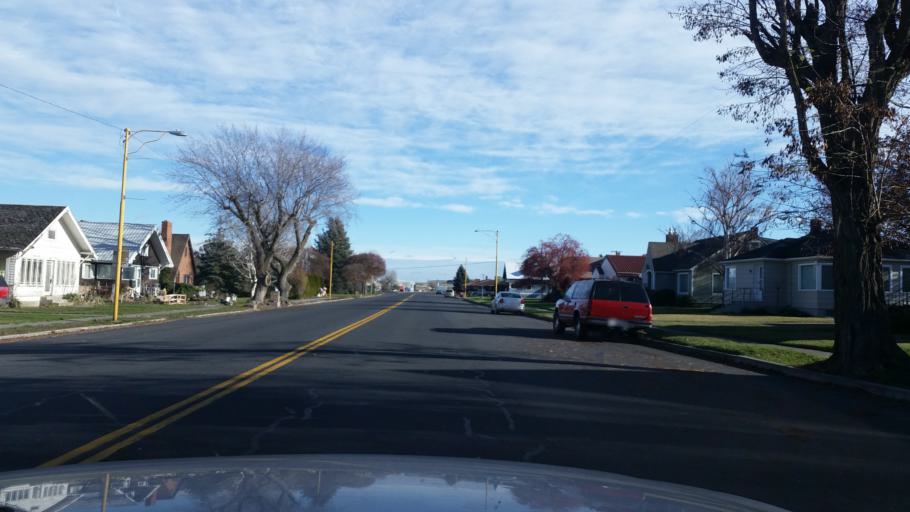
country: US
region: Washington
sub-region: Adams County
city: Ritzville
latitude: 47.3330
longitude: -118.6824
